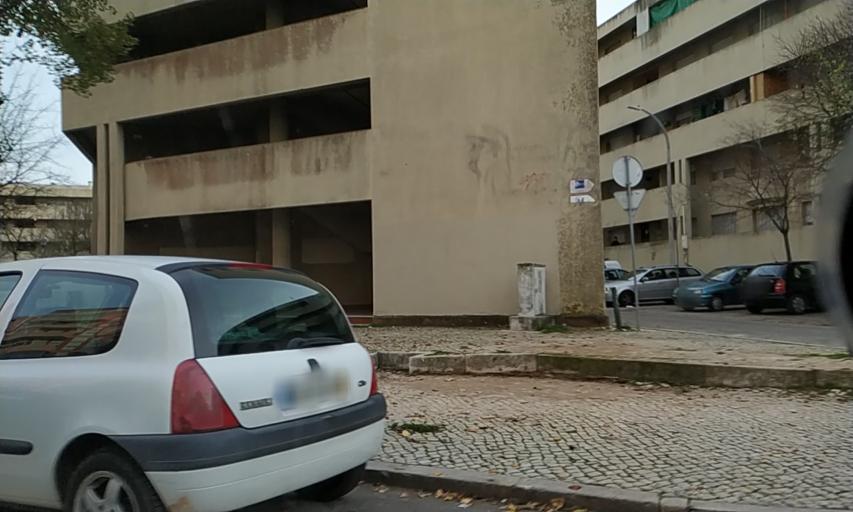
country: PT
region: Setubal
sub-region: Setubal
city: Setubal
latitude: 38.5300
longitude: -8.8773
